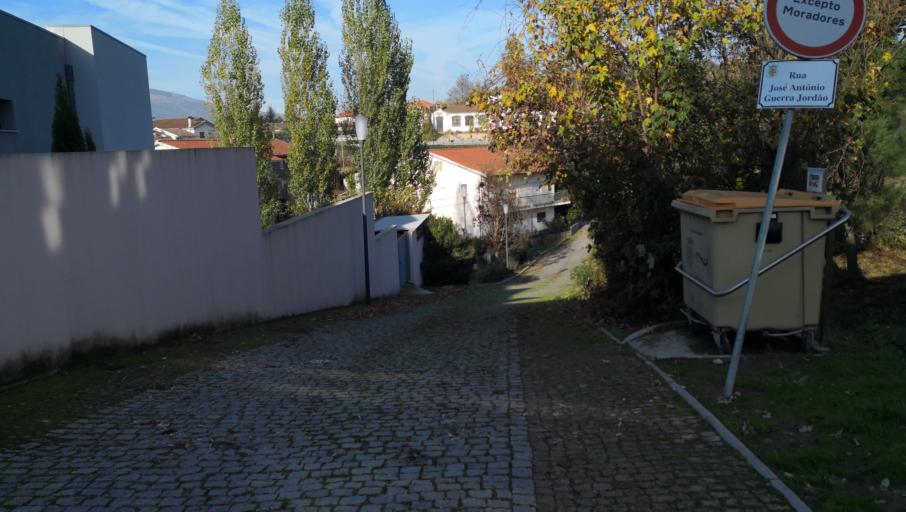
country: PT
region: Vila Real
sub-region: Vila Real
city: Vila Real
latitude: 41.3006
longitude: -7.7186
